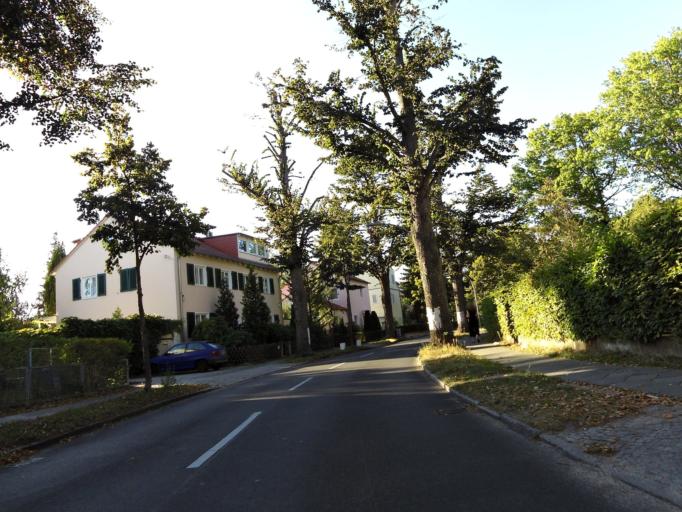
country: DE
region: Berlin
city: Dahlem
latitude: 52.4486
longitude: 13.2758
